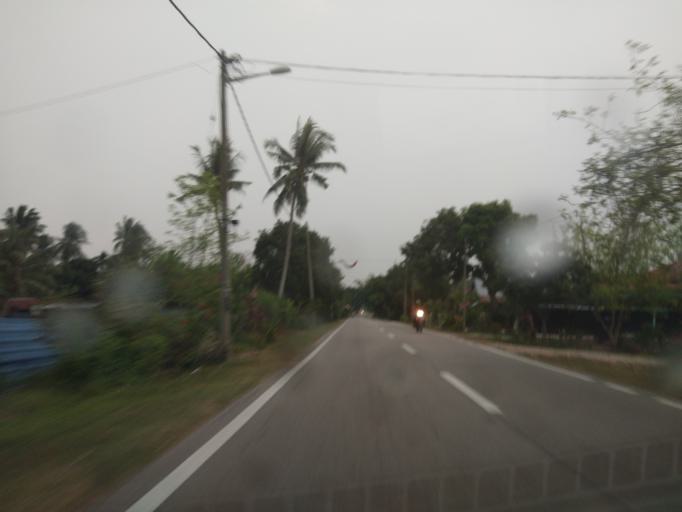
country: MY
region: Penang
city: Kepala Batas
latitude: 5.4982
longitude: 100.3964
